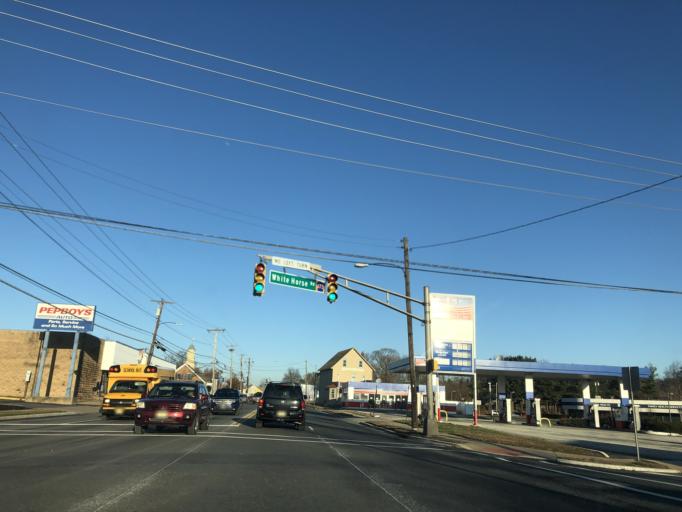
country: US
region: New Jersey
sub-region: Camden County
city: Stratford
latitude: 39.8336
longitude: -75.0055
